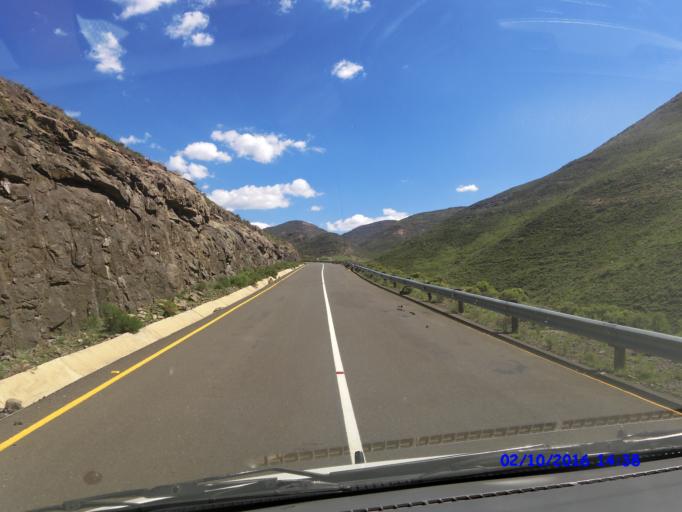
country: LS
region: Maseru
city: Nako
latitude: -29.5118
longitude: 28.0629
